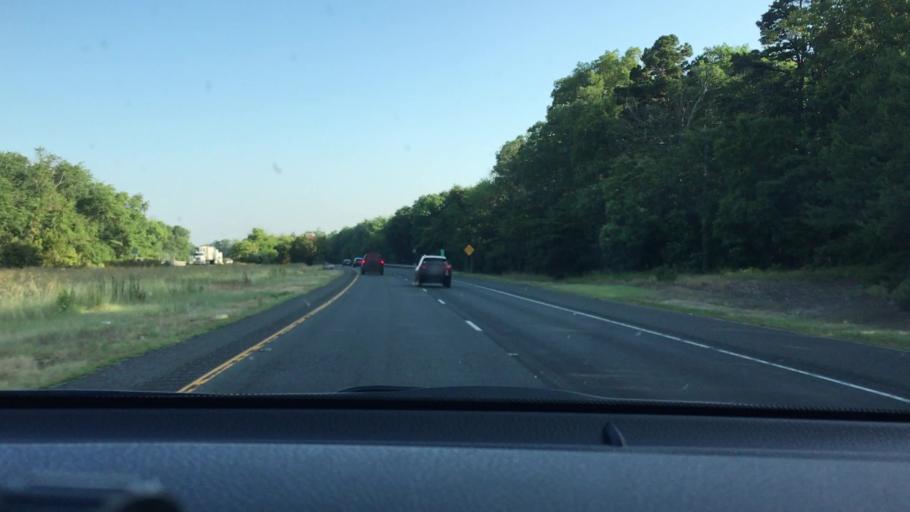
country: US
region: New Jersey
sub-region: Gloucester County
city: Newfield
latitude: 39.5659
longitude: -75.0610
